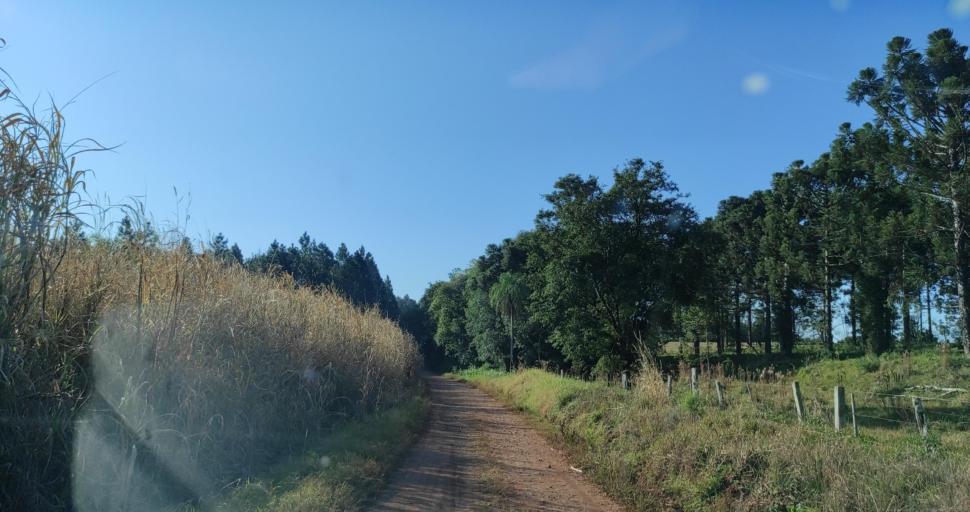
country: AR
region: Misiones
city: Capiovi
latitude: -26.8933
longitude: -55.1072
